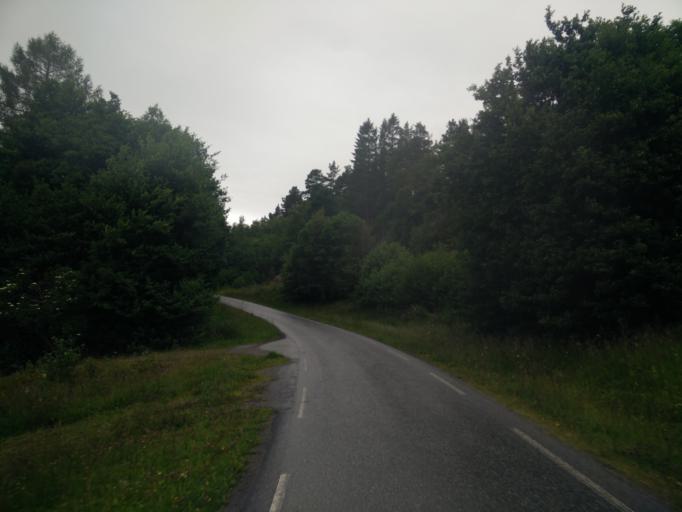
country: NO
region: More og Romsdal
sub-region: Kristiansund
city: Rensvik
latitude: 63.0182
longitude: 7.9026
